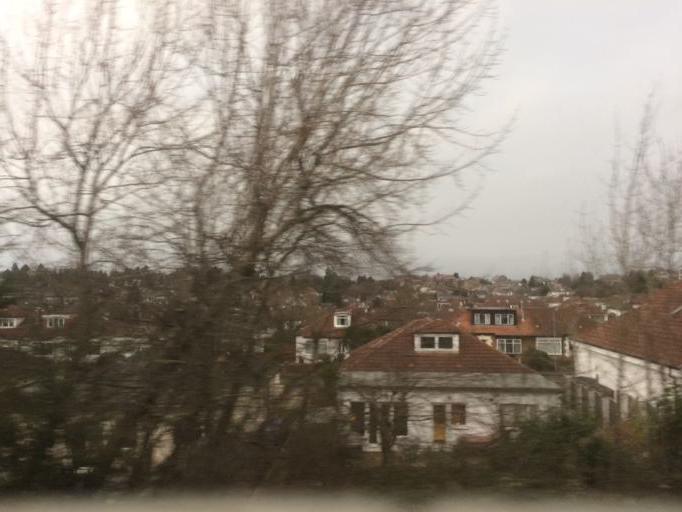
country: GB
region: Scotland
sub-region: East Renfrewshire
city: Giffnock
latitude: 55.7954
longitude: -4.2878
